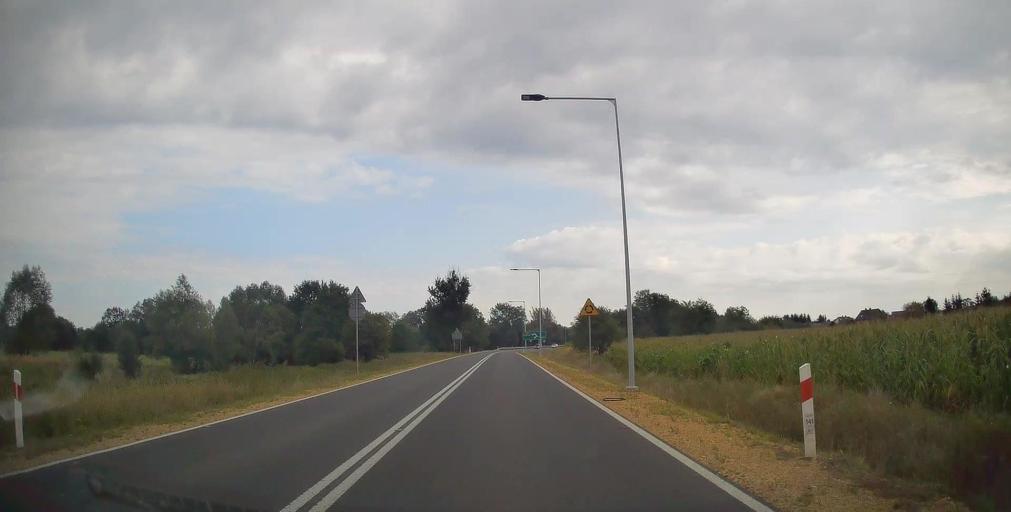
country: PL
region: Lesser Poland Voivodeship
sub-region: Powiat oswiecimski
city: Zator
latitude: 50.0214
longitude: 19.4322
